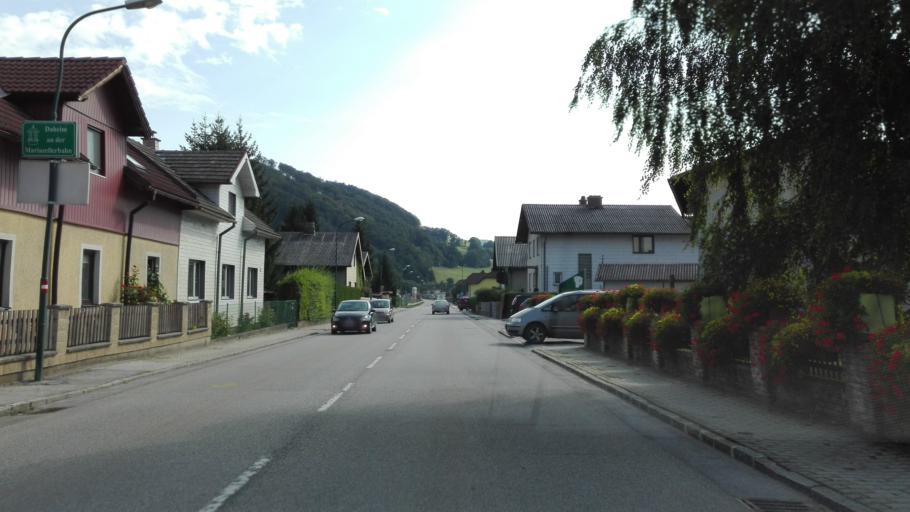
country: AT
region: Lower Austria
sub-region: Politischer Bezirk Sankt Polten
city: Rabenstein an der Pielach
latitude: 48.0669
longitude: 15.4743
